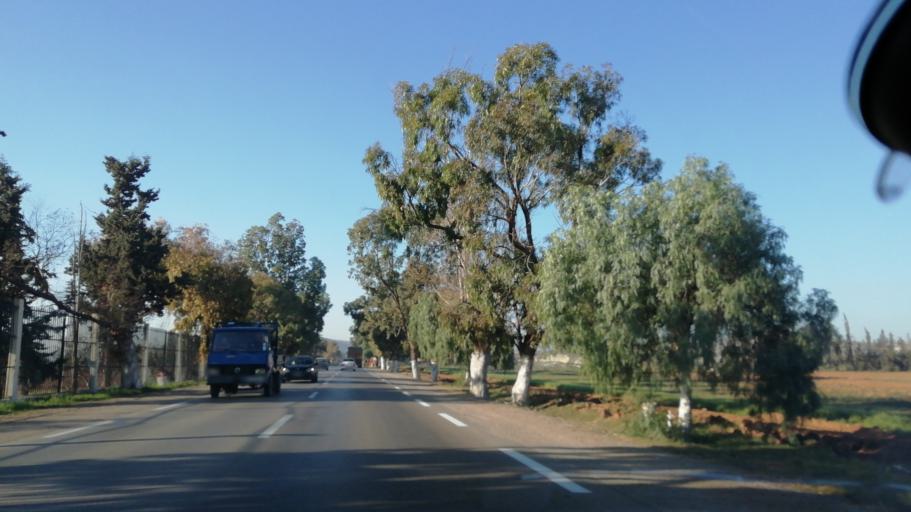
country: DZ
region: Tlemcen
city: Remchi
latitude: 35.0585
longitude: -1.4950
